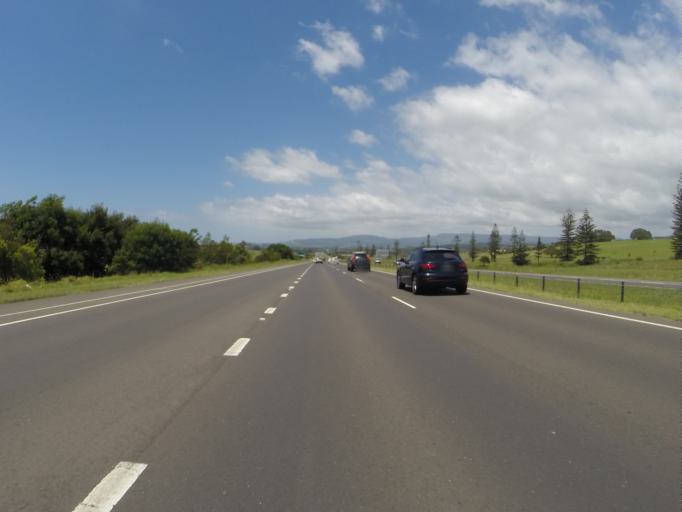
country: AU
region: New South Wales
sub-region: Shellharbour
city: Croom
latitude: -34.5927
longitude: 150.8436
